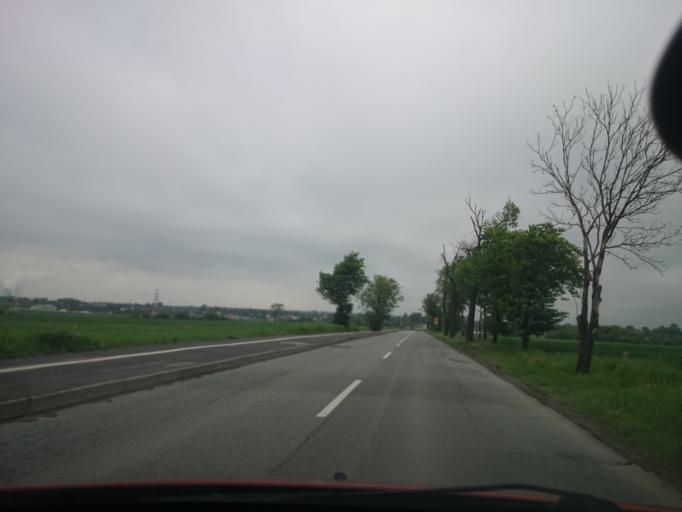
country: PL
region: Opole Voivodeship
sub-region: Powiat opolski
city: Opole
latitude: 50.6978
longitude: 17.9291
